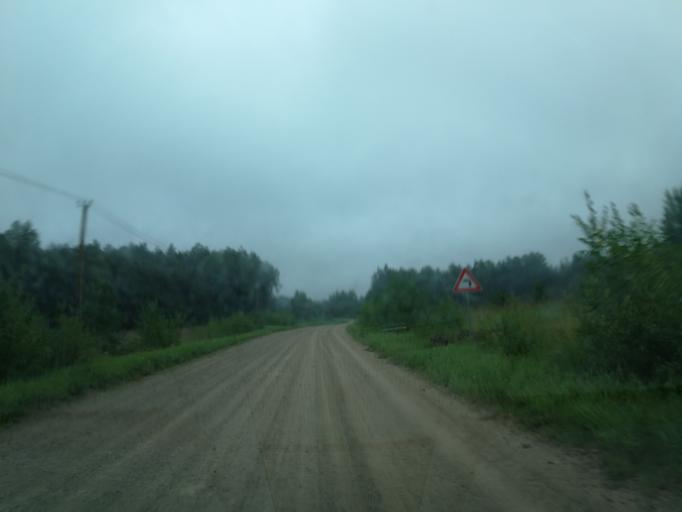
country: LV
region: Preilu Rajons
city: Jaunaglona
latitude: 56.3455
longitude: 27.0047
